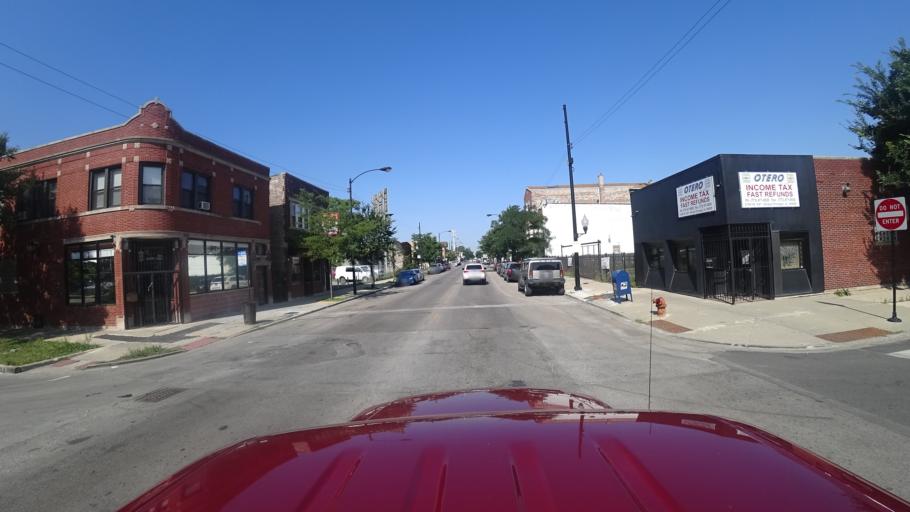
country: US
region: Illinois
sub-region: Cook County
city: Hometown
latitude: 41.7865
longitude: -87.6911
